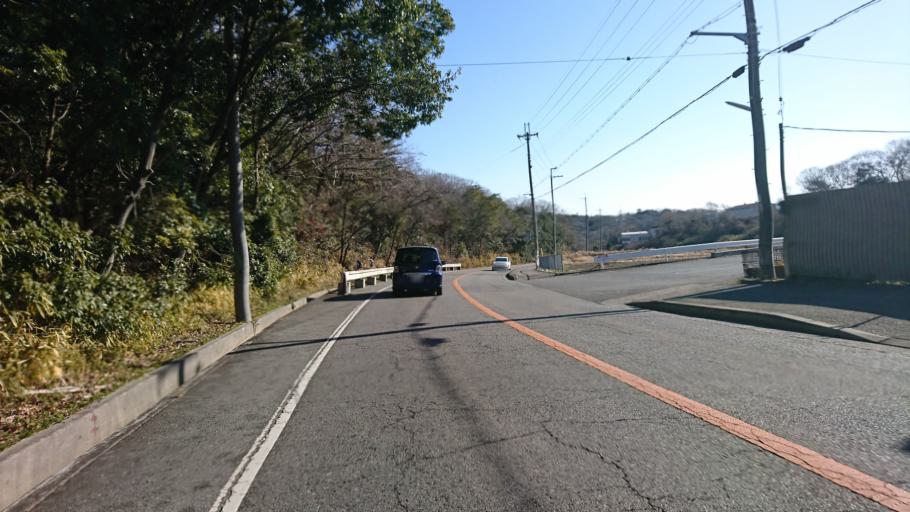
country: JP
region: Hyogo
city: Akashi
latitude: 34.7155
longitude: 134.9689
